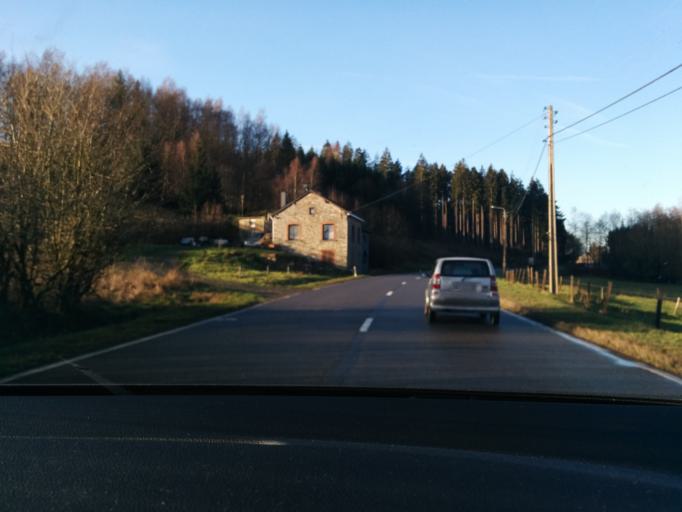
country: BE
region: Wallonia
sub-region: Province du Luxembourg
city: Vielsalm
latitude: 50.2682
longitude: 5.8875
